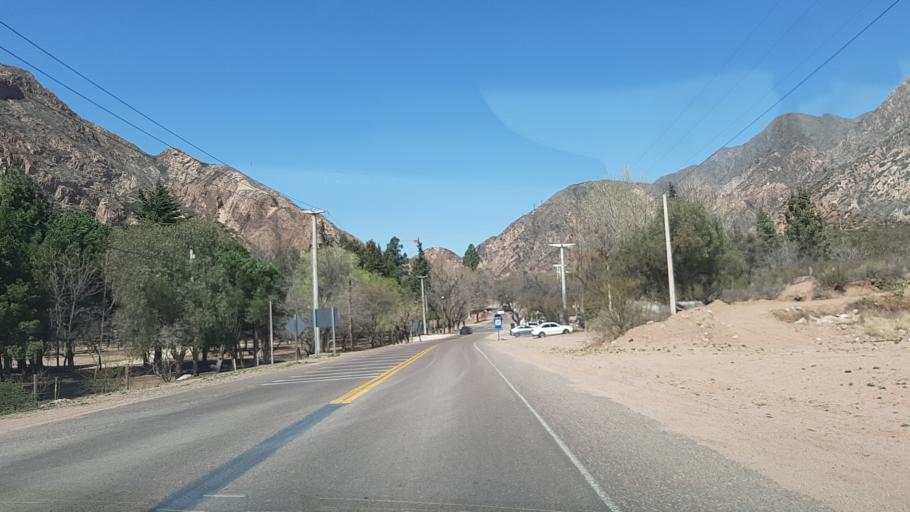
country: AR
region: Mendoza
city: Lujan de Cuyo
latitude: -33.0177
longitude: -69.1175
